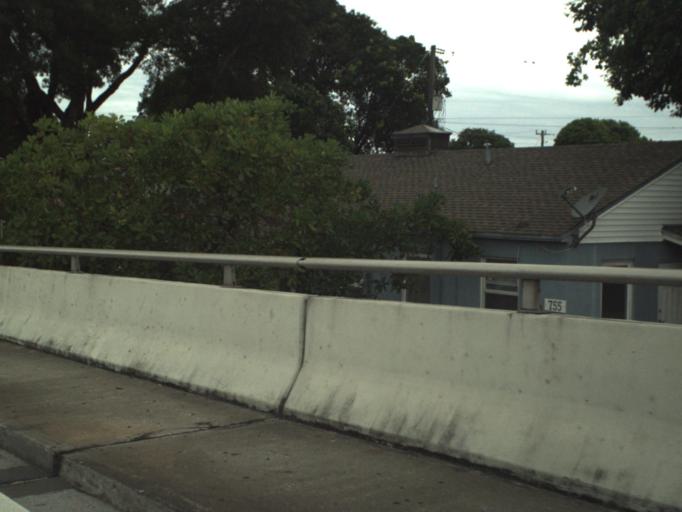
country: US
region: Florida
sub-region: Palm Beach County
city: Lake Clarke Shores
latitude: 26.6759
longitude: -80.0598
